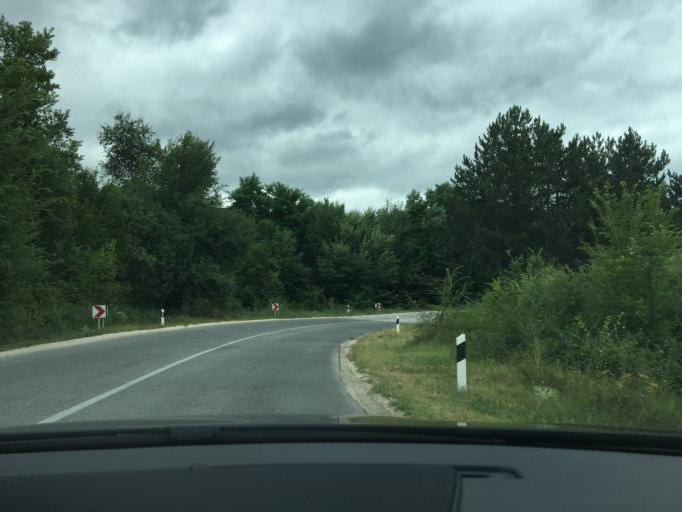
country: MK
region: Kriva Palanka
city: Kriva Palanka
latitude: 42.1858
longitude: 22.2810
